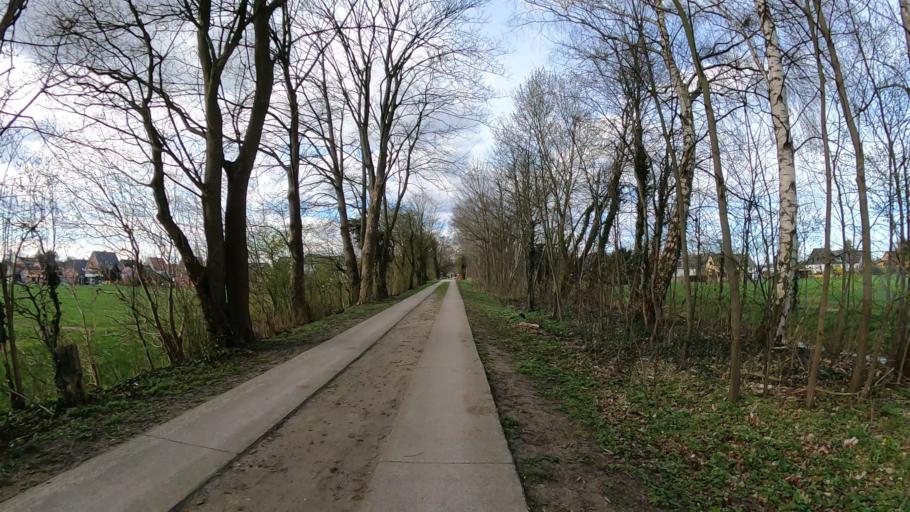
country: DE
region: Hamburg
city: Rothenburgsort
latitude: 53.4715
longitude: 10.0872
